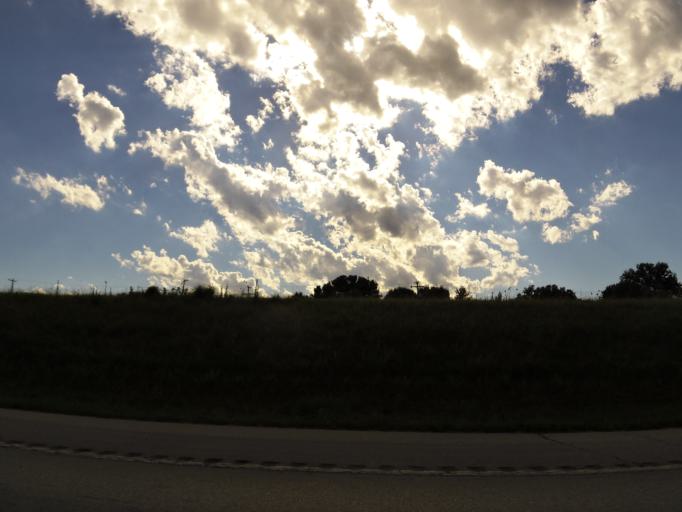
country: US
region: Missouri
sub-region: Marion County
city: Palmyra
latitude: 39.7916
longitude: -91.5174
